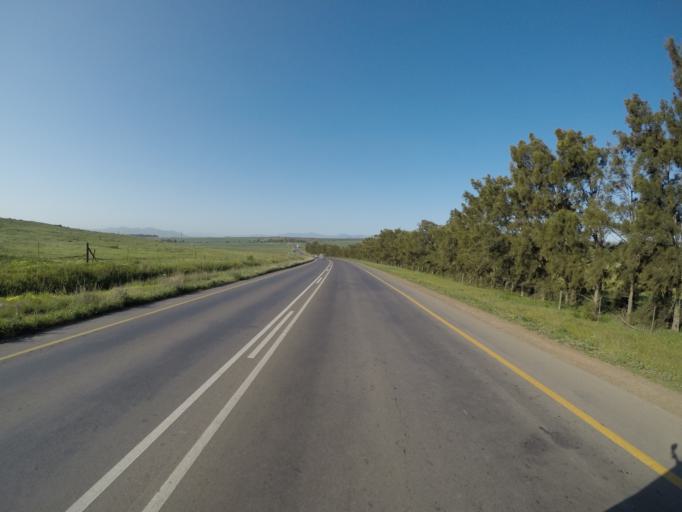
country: ZA
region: Western Cape
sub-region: City of Cape Town
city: Kraaifontein
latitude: -33.7733
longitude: 18.7513
